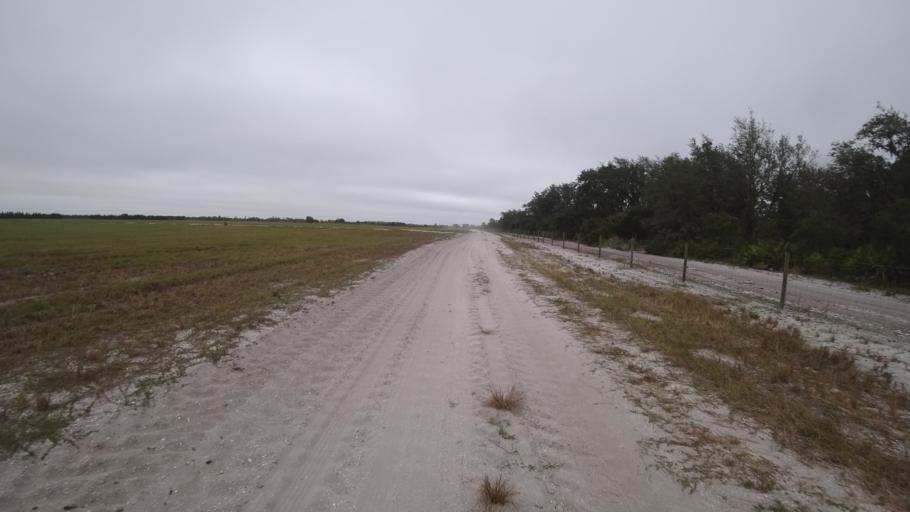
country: US
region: Florida
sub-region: Sarasota County
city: Warm Mineral Springs
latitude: 27.2863
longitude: -82.1346
